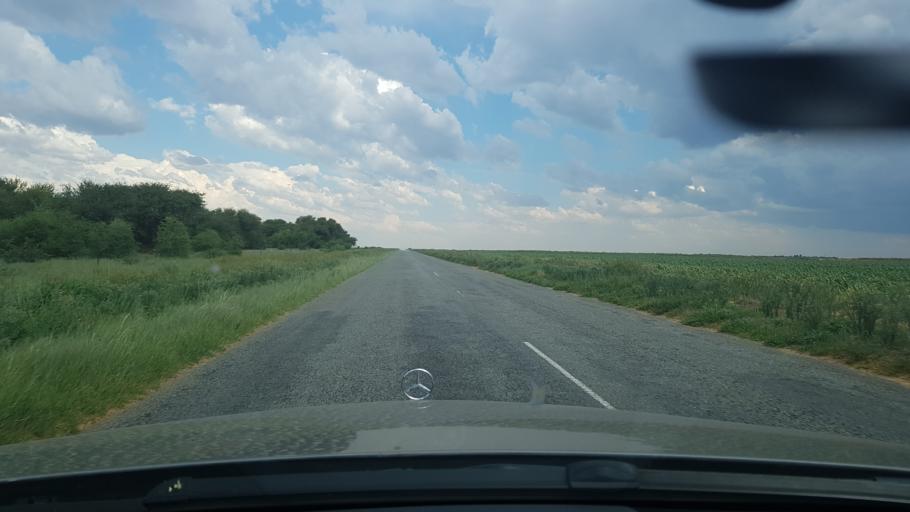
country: ZA
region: North-West
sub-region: Dr Ruth Segomotsi Mompati District Municipality
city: Bloemhof
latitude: -27.8741
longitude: 25.6602
